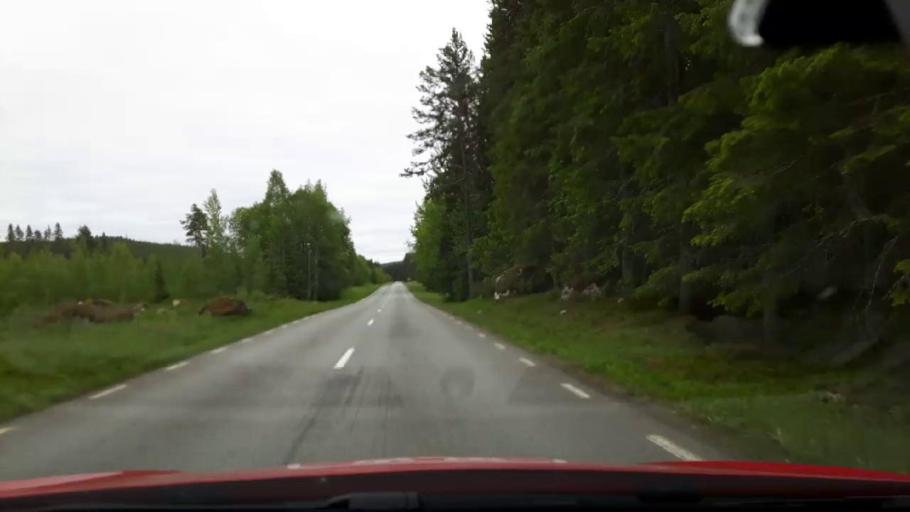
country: SE
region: Jaemtland
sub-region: Stroemsunds Kommun
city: Stroemsund
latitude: 63.4404
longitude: 15.4839
